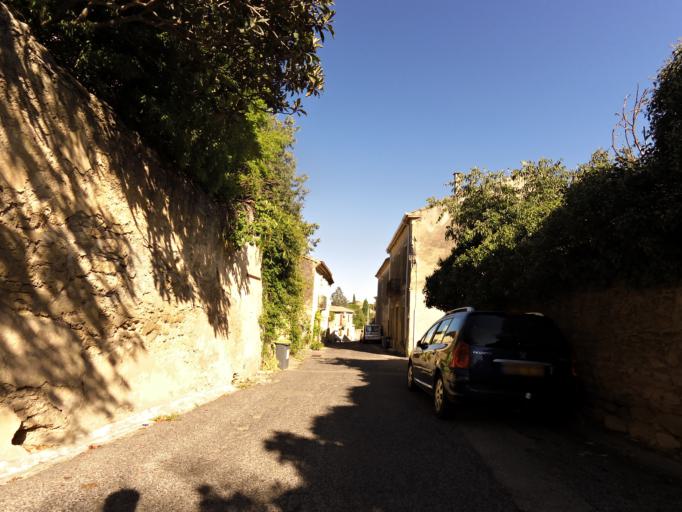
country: FR
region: Languedoc-Roussillon
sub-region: Departement du Gard
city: Aubais
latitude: 43.7544
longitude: 4.1500
